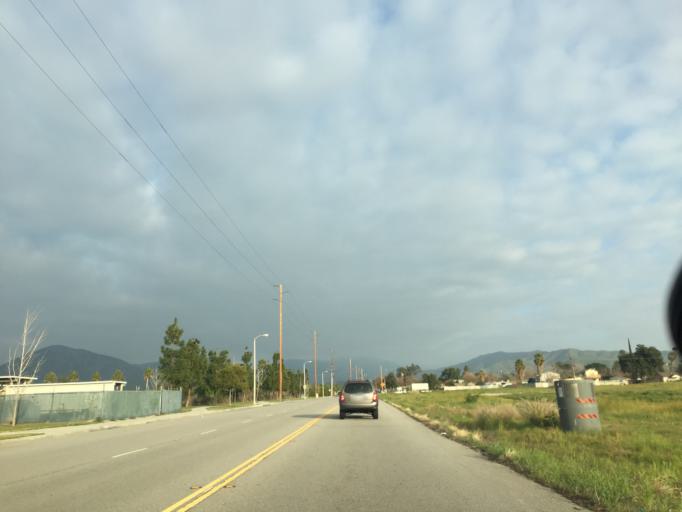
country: US
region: California
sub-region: San Bernardino County
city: Mentone
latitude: 34.0774
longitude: -117.1414
